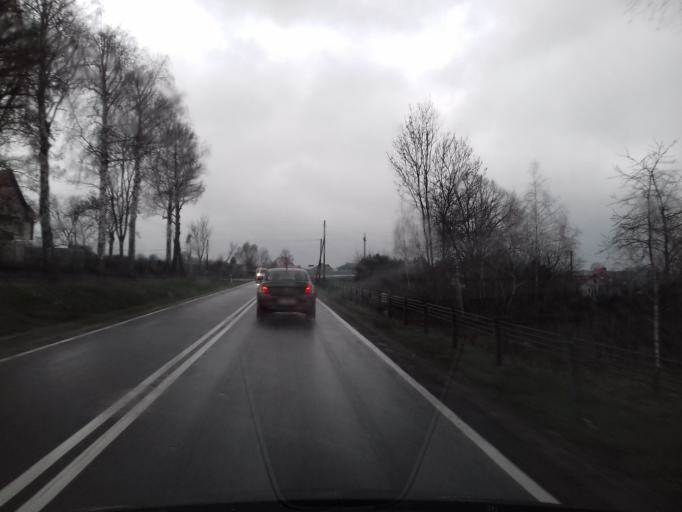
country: PL
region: Lesser Poland Voivodeship
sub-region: Powiat nowosadecki
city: Chelmiec
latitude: 49.6348
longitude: 20.6252
